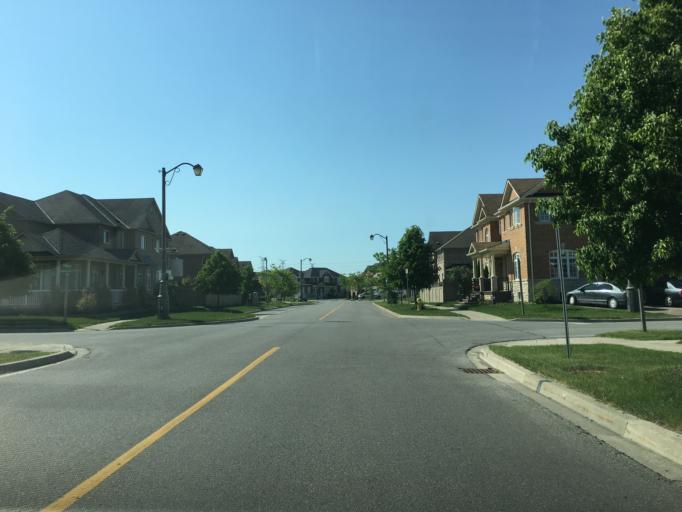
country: CA
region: Ontario
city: Markham
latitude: 43.8548
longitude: -79.2264
